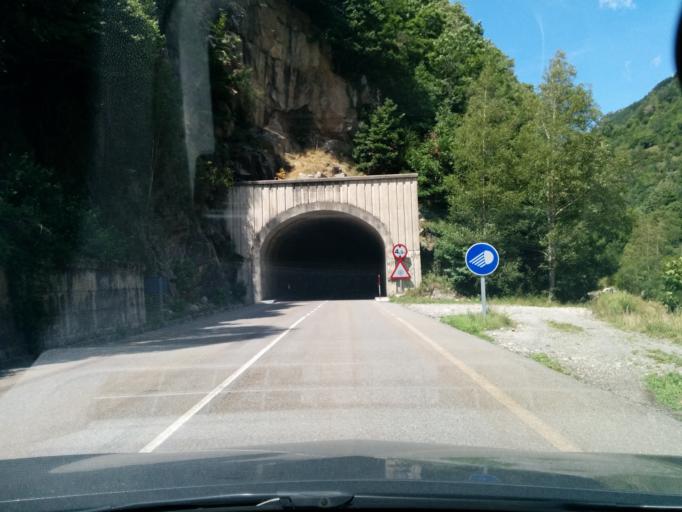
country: ES
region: Aragon
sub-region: Provincia de Huesca
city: Bielsa
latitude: 42.6393
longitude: 0.2151
